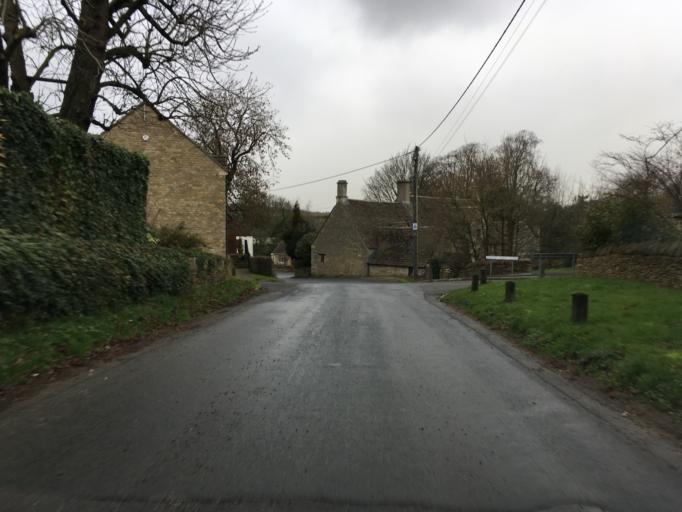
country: GB
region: England
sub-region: Wiltshire
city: Nettleton
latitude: 51.5138
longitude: -2.2647
